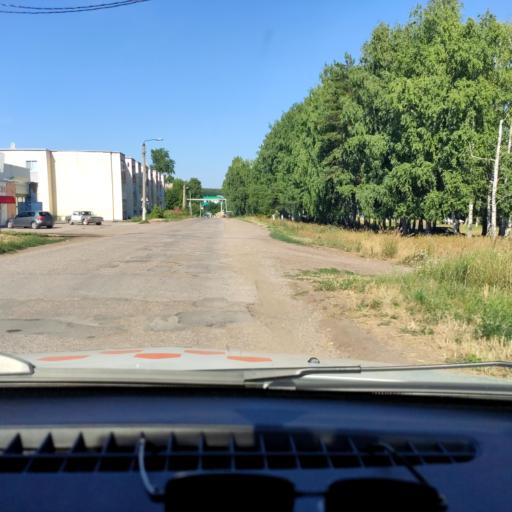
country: RU
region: Bashkortostan
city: Tolbazy
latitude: 54.0054
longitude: 55.8896
